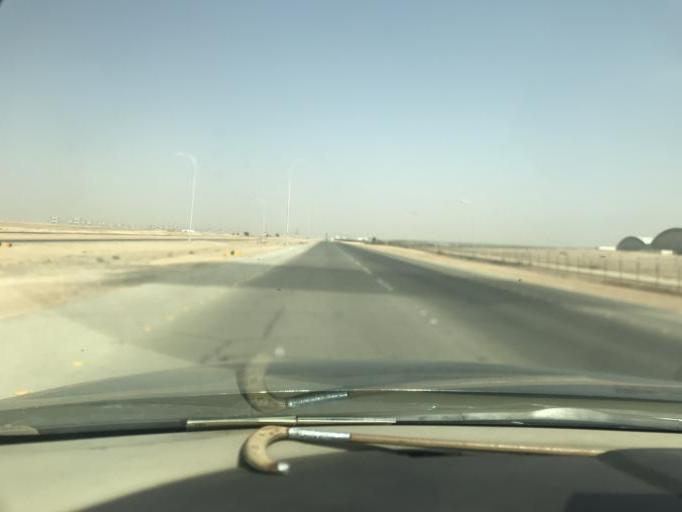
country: SA
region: Ar Riyad
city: Riyadh
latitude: 24.9596
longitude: 46.6701
